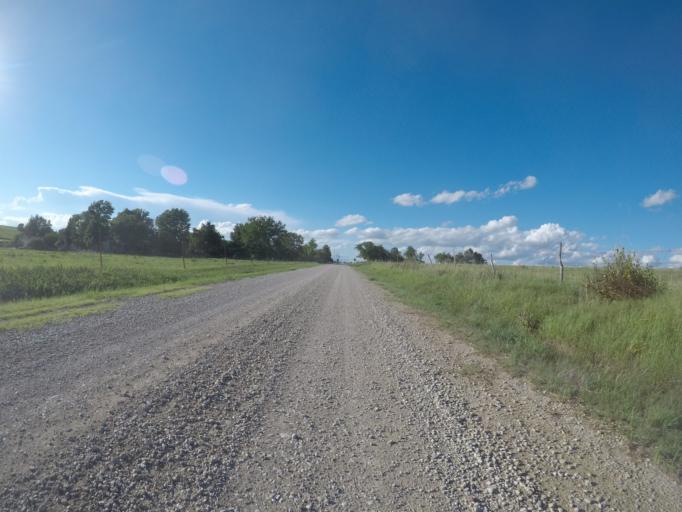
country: US
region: Kansas
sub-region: Riley County
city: Ogden
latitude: 39.2596
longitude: -96.7378
